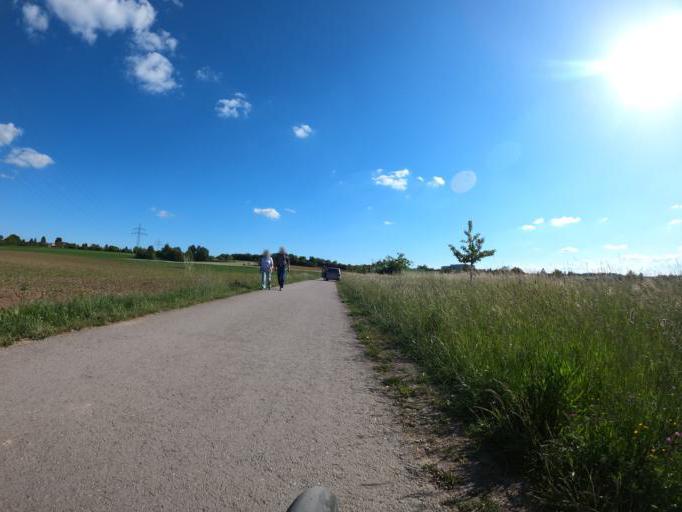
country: DE
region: Baden-Wuerttemberg
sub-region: Regierungsbezirk Stuttgart
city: Magstadt
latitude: 48.7358
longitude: 8.9793
